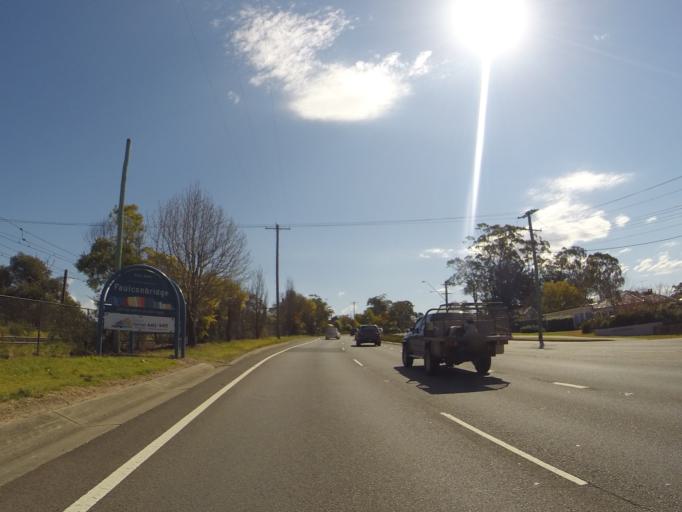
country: AU
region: New South Wales
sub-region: Blue Mountains Municipality
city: Blaxland
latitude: -33.6963
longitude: 150.5498
